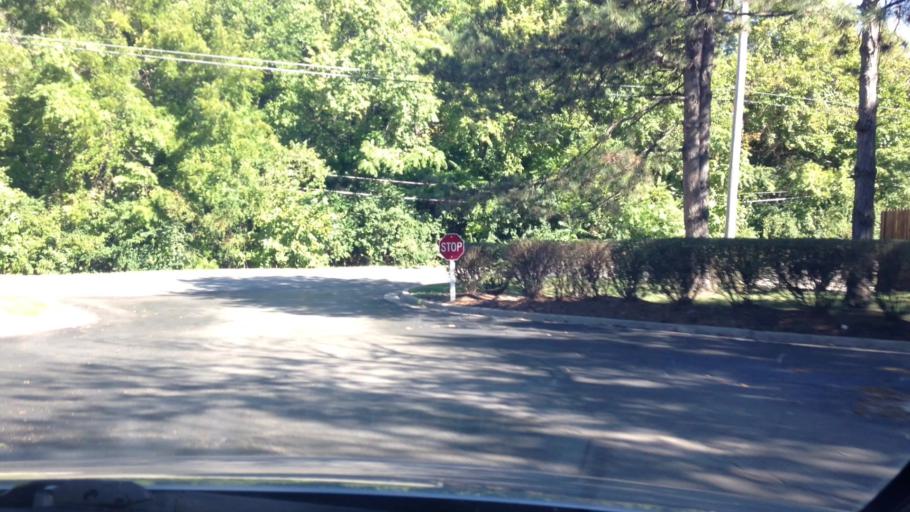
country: US
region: Kansas
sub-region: Johnson County
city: Roeland Park
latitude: 39.0446
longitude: -94.6403
